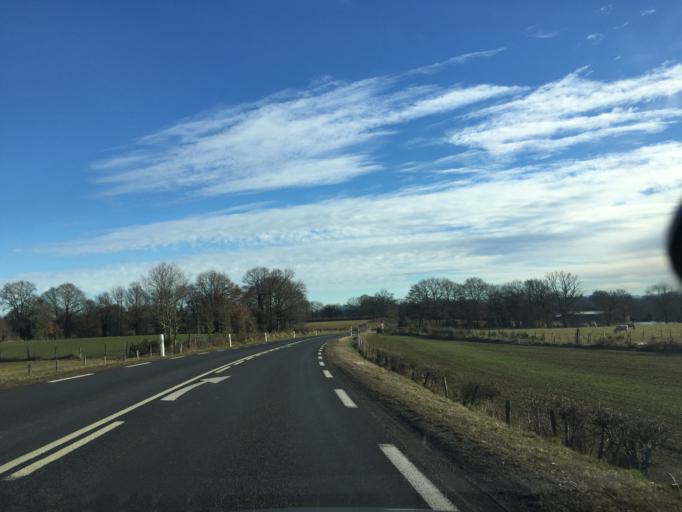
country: FR
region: Limousin
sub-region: Departement de la Creuse
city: Auzances
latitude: 45.8672
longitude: 2.5547
